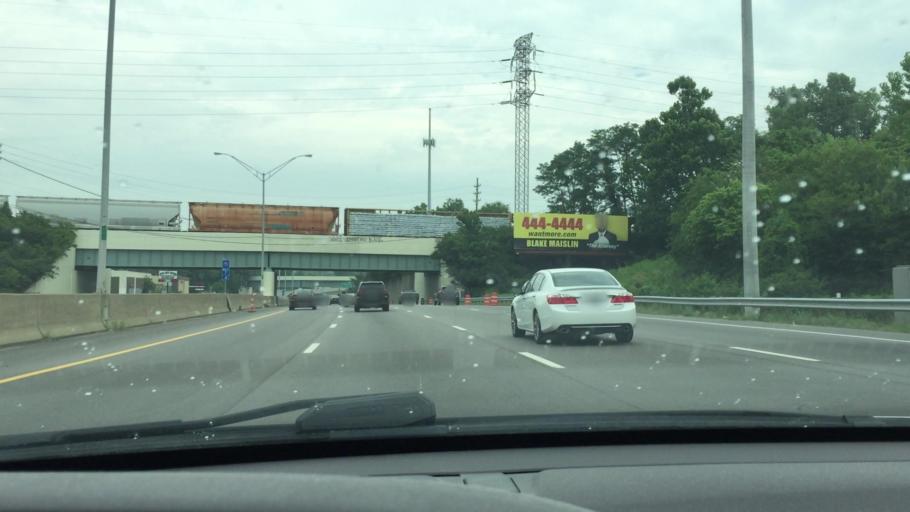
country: US
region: Ohio
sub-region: Hamilton County
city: Cincinnati
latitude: 39.1583
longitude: -84.4384
